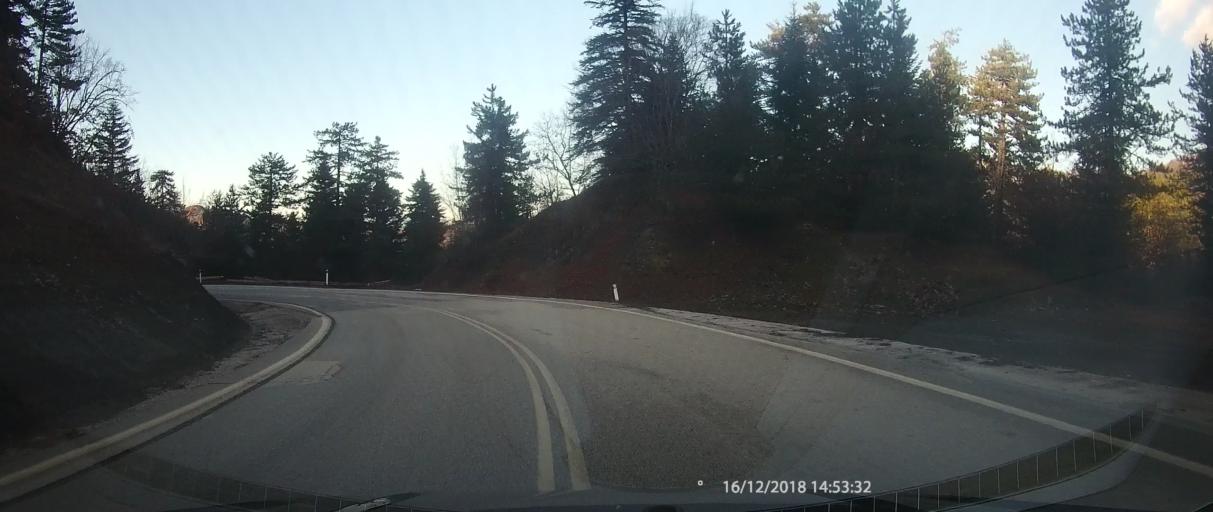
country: GR
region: West Macedonia
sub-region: Nomos Kastorias
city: Nestorio
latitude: 40.2104
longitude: 21.0571
